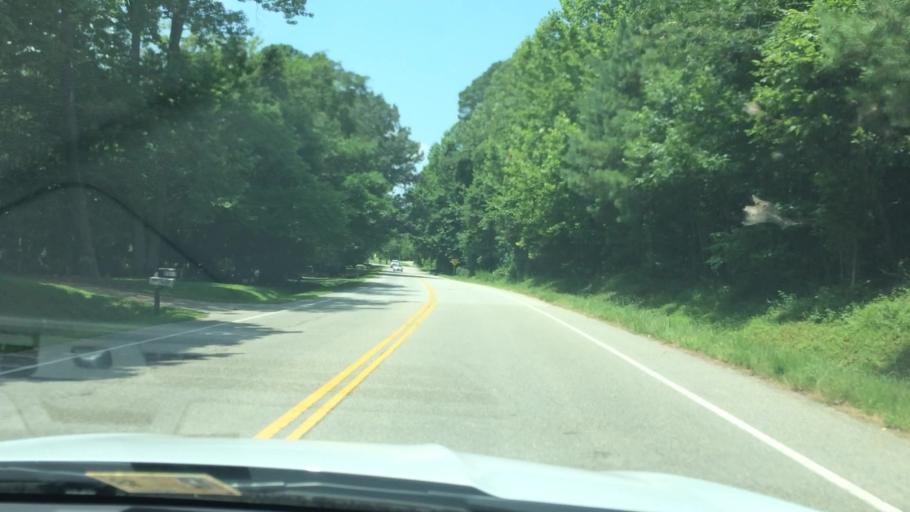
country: US
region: Virginia
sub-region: York County
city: Yorktown
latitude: 37.2057
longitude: -76.4945
